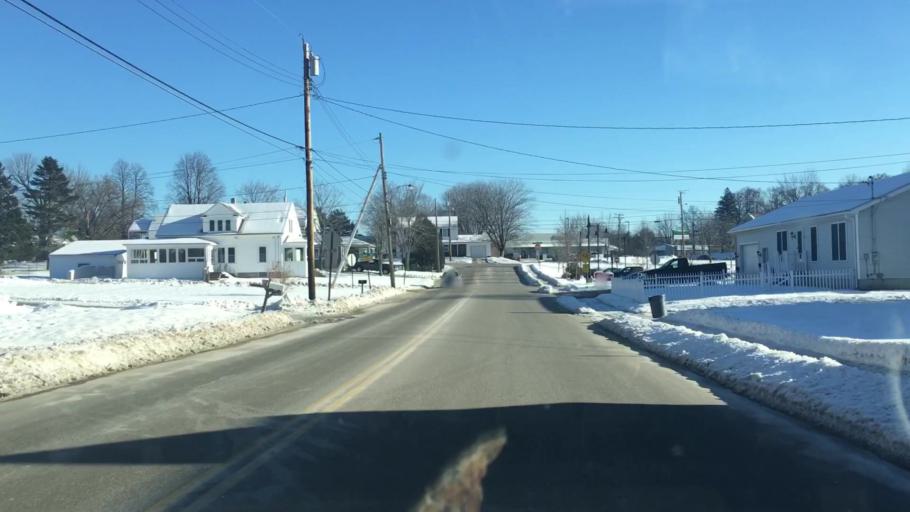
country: US
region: Maine
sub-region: Androscoggin County
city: Lewiston
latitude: 44.1045
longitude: -70.1750
